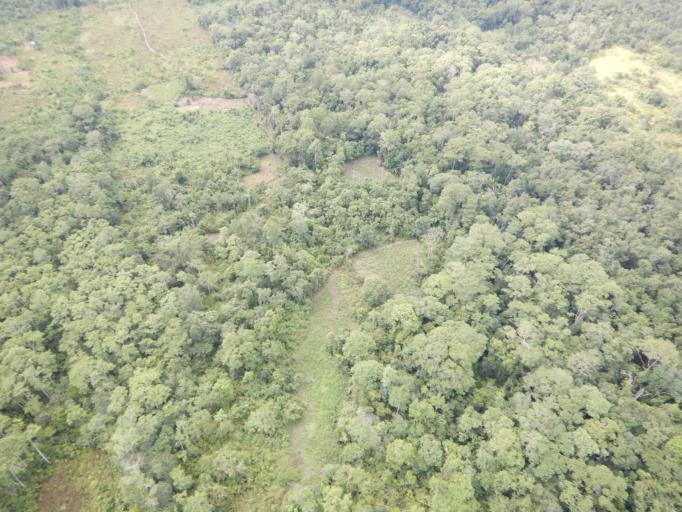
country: BO
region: Cochabamba
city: Chimore
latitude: -16.9699
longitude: -65.0312
